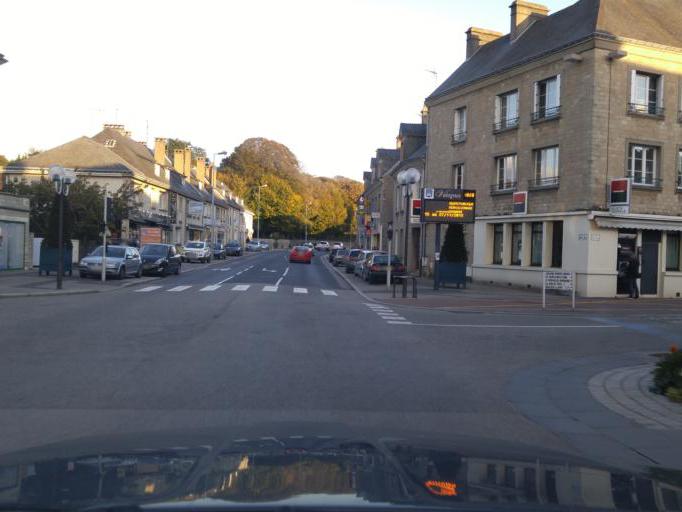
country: FR
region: Lower Normandy
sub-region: Departement de la Manche
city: Valognes
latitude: 49.5090
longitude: -1.4695
